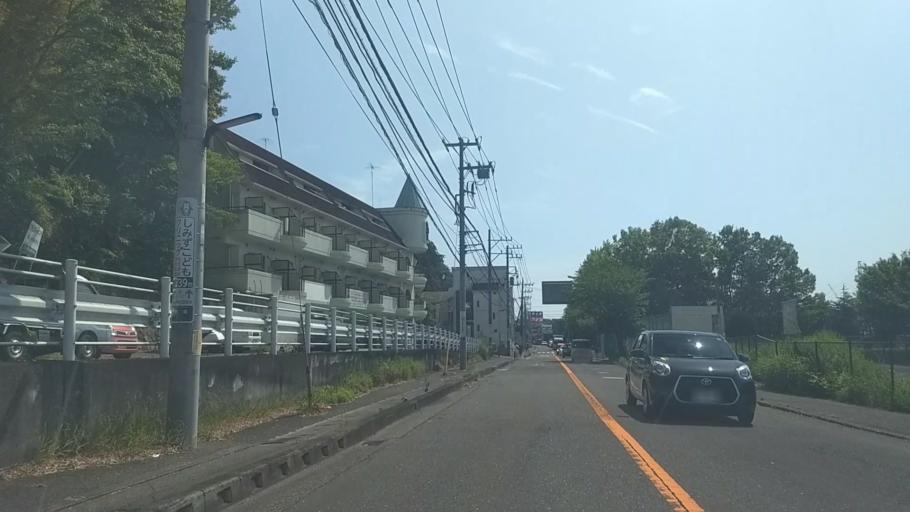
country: JP
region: Kanagawa
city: Kamakura
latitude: 35.3599
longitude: 139.5479
